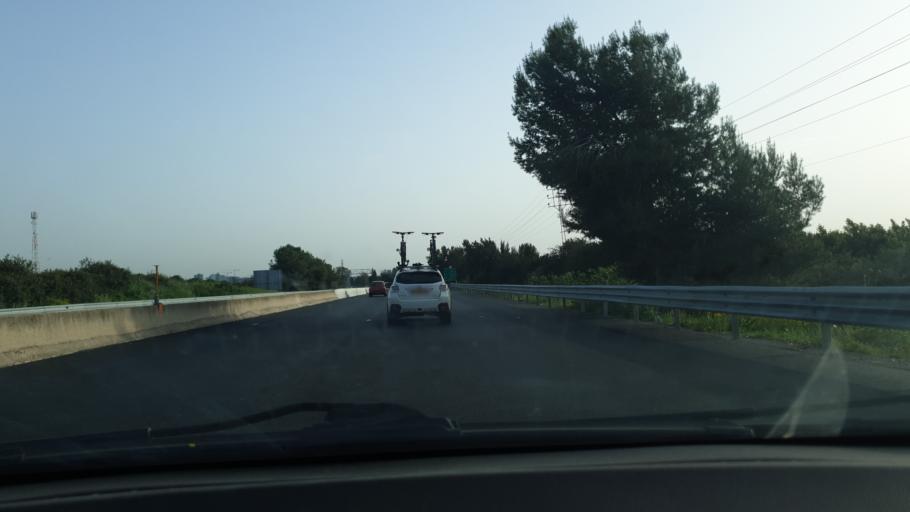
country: IL
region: Central District
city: Tel Mond
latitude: 32.2300
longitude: 34.8837
